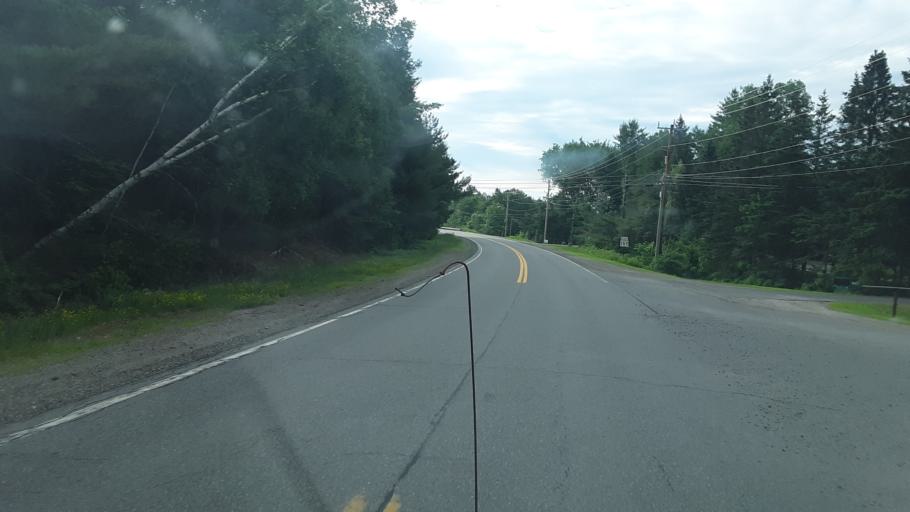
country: US
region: Maine
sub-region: Penobscot County
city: Medway
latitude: 45.6014
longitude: -68.5179
